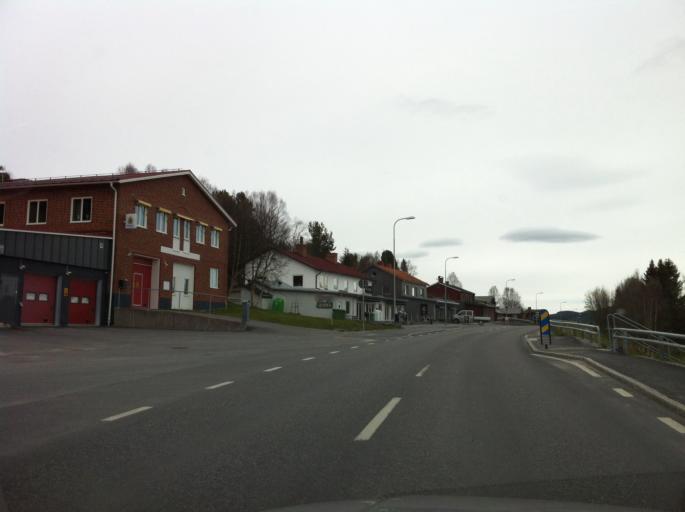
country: NO
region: Hedmark
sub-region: Engerdal
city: Engerdal
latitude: 62.5452
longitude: 12.5450
